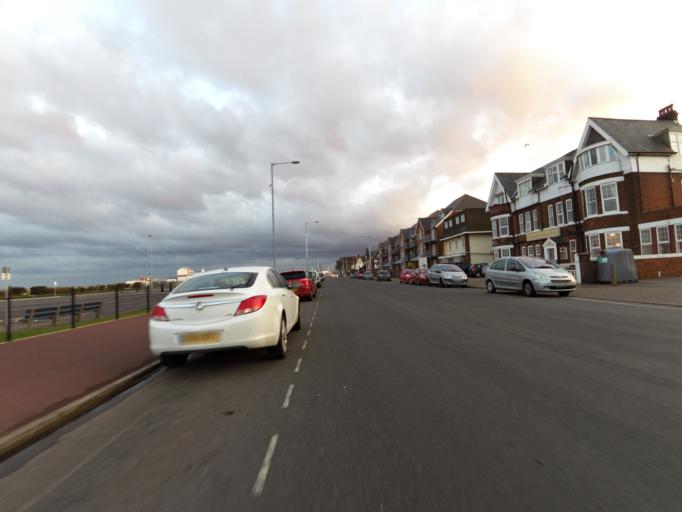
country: GB
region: England
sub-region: Norfolk
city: Great Yarmouth
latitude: 52.6123
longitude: 1.7378
